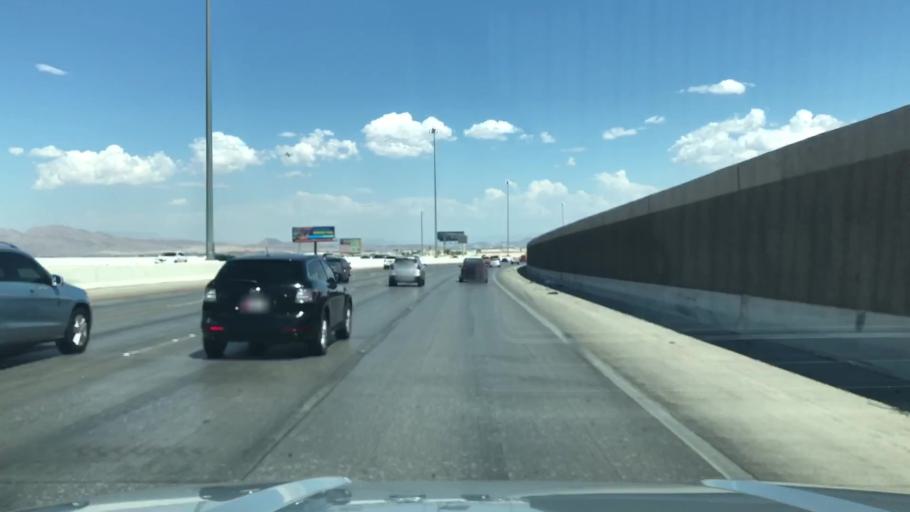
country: US
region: Nevada
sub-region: Clark County
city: Spring Valley
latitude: 36.0683
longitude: -115.2027
